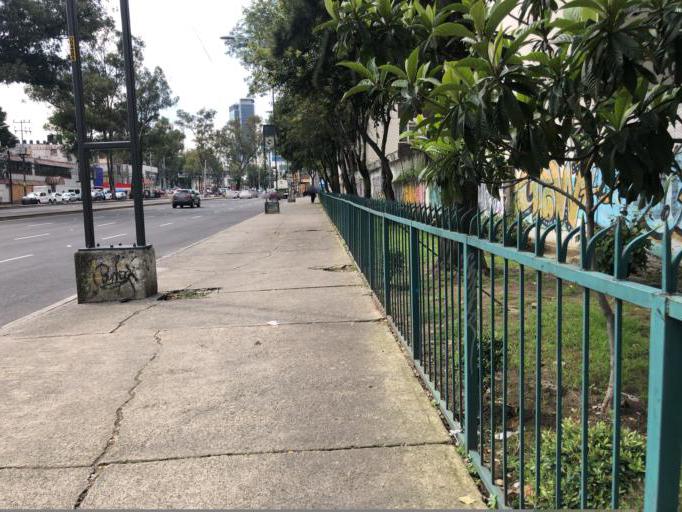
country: MX
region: Mexico City
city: Coyoacan
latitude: 19.3370
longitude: -99.1823
